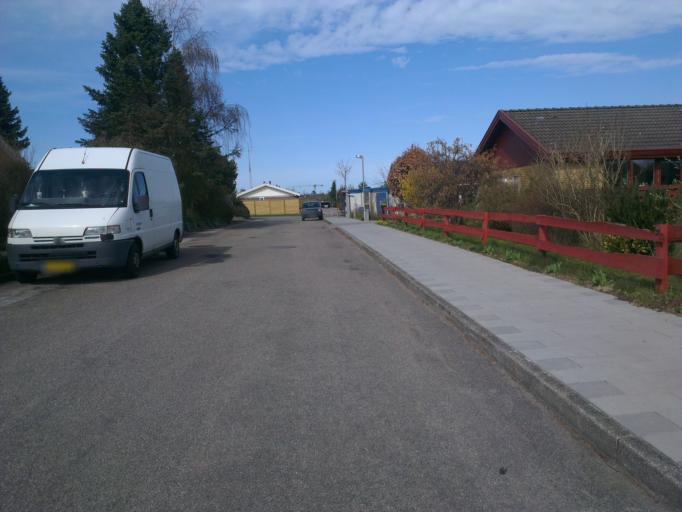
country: DK
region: Capital Region
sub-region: Frederikssund Kommune
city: Frederikssund
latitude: 55.8236
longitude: 12.0715
